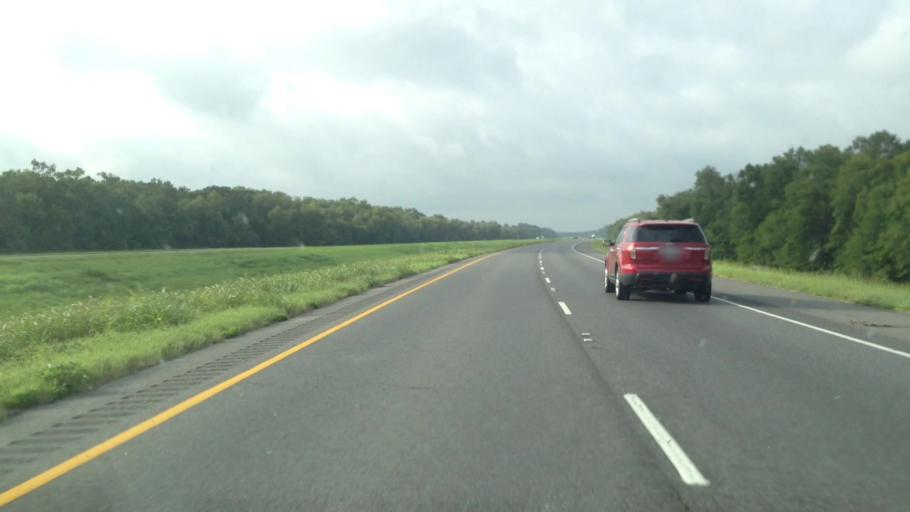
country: US
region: Louisiana
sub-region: Saint Landry Parish
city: Opelousas
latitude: 30.6907
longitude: -92.0804
